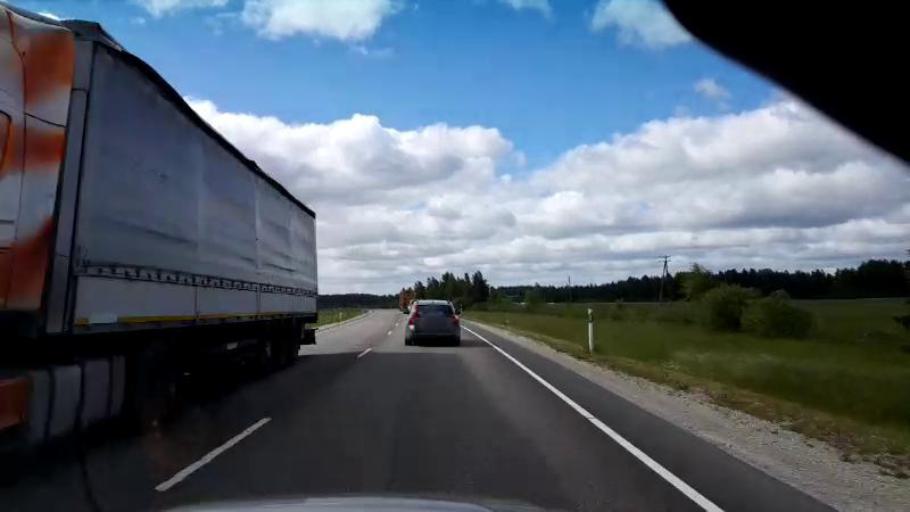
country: EE
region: Paernumaa
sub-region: Sauga vald
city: Sauga
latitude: 58.4873
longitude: 24.5284
